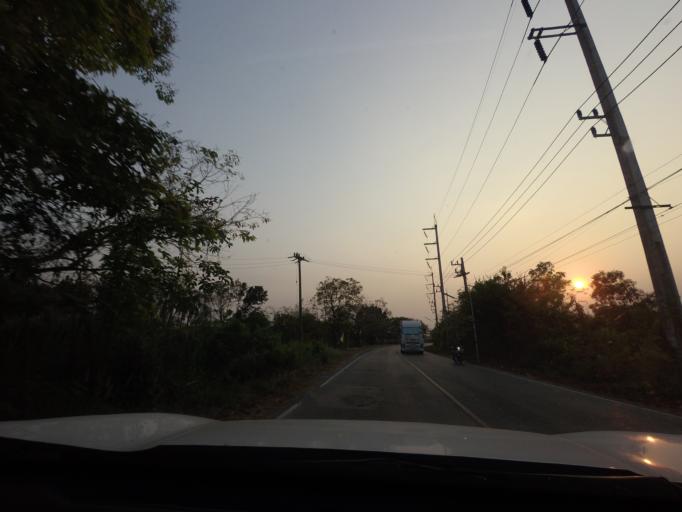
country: TH
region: Nakhon Nayok
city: Ongkharak
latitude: 14.1154
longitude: 101.0220
